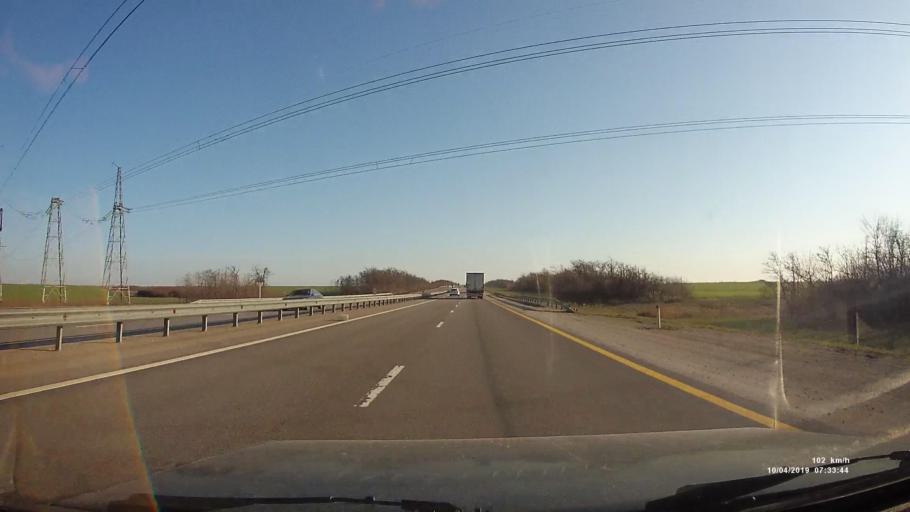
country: RU
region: Rostov
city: Likhoy
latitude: 48.0168
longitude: 40.2436
